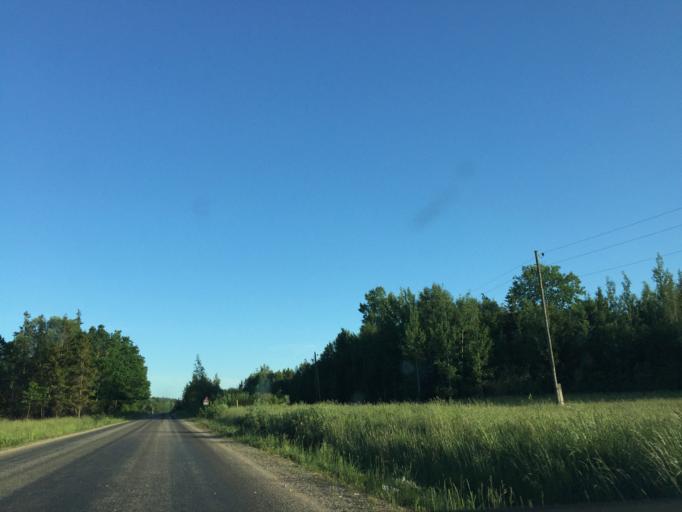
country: LV
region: Broceni
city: Broceni
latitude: 56.7134
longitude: 22.5022
